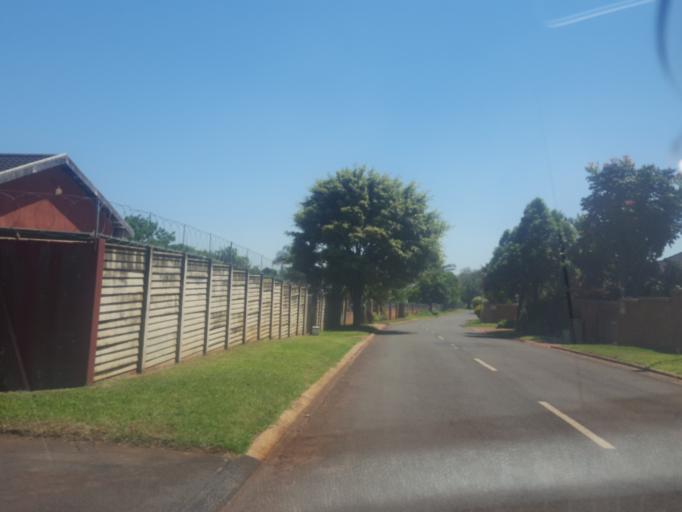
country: ZA
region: KwaZulu-Natal
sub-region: uThungulu District Municipality
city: Empangeni
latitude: -28.7475
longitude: 31.9070
